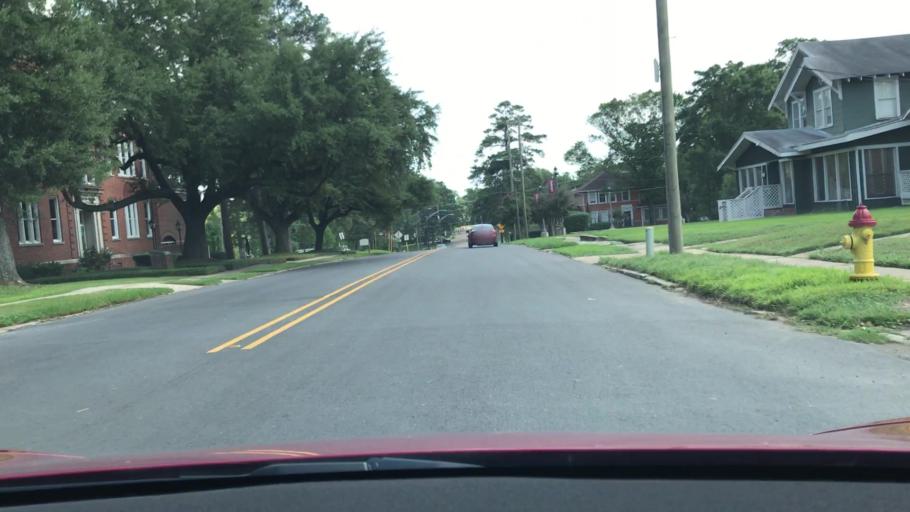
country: US
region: Louisiana
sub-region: Bossier Parish
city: Bossier City
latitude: 32.4838
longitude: -93.7339
